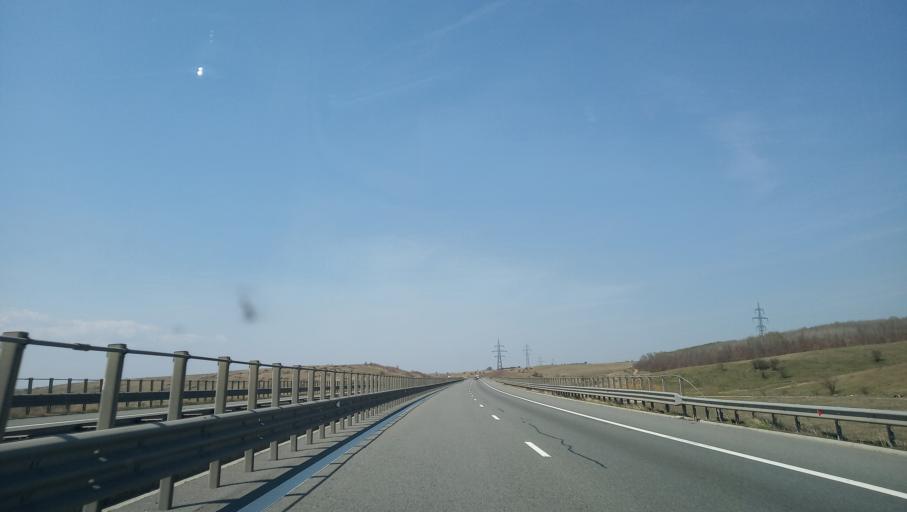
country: RO
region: Cluj
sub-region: Comuna Ciurila
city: Ciurila
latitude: 46.6451
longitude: 23.5164
